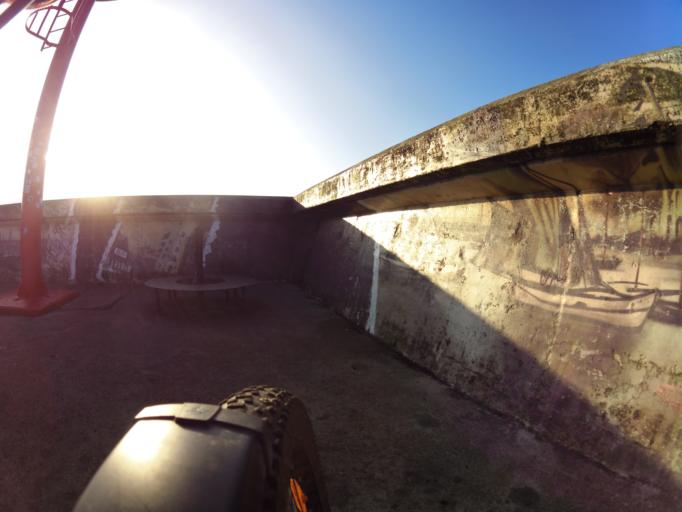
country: PL
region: Pomeranian Voivodeship
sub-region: Powiat pucki
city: Hel
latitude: 54.5996
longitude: 18.7997
